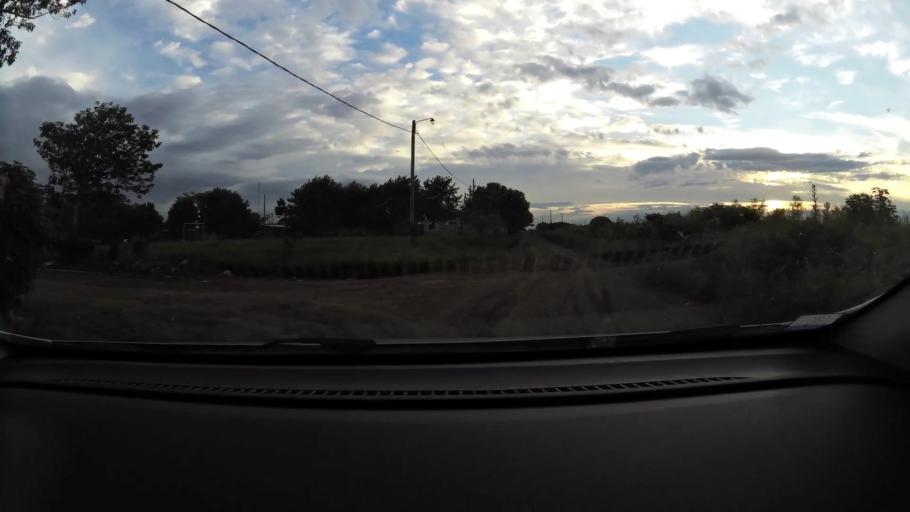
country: AR
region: Buenos Aires
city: San Nicolas de los Arroyos
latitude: -33.3152
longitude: -60.2433
